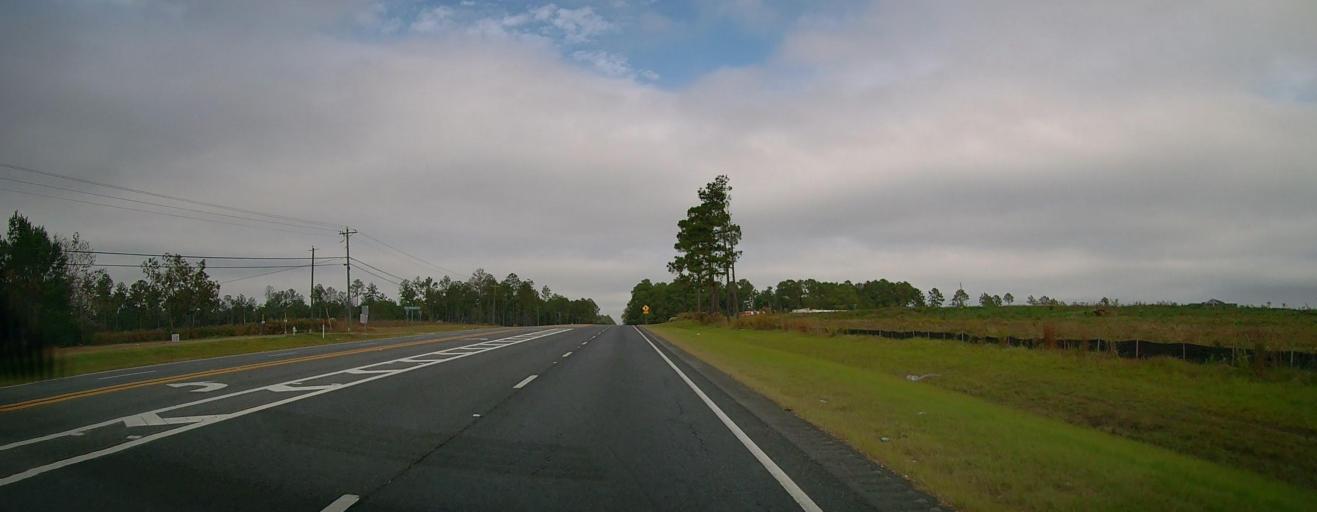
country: US
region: Georgia
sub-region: Tift County
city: Unionville
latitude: 31.4195
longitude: -83.5353
